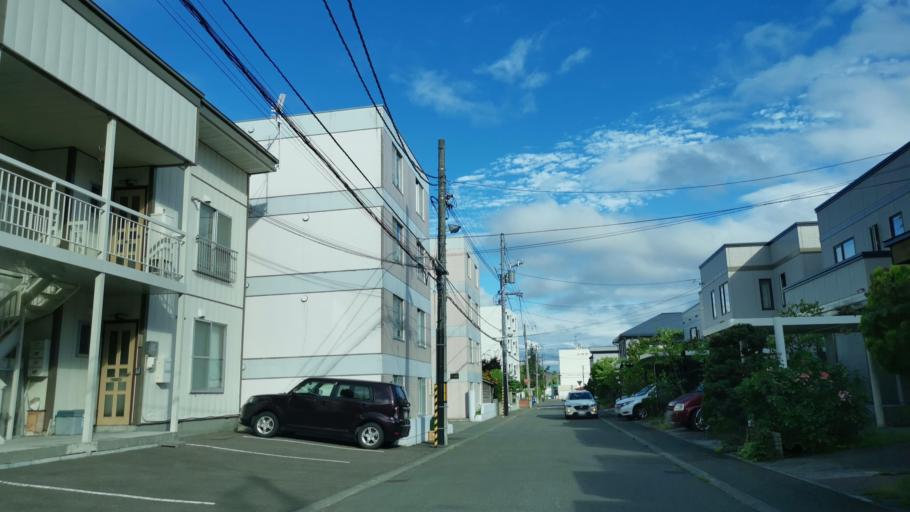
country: JP
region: Hokkaido
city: Sapporo
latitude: 43.0633
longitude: 141.2963
